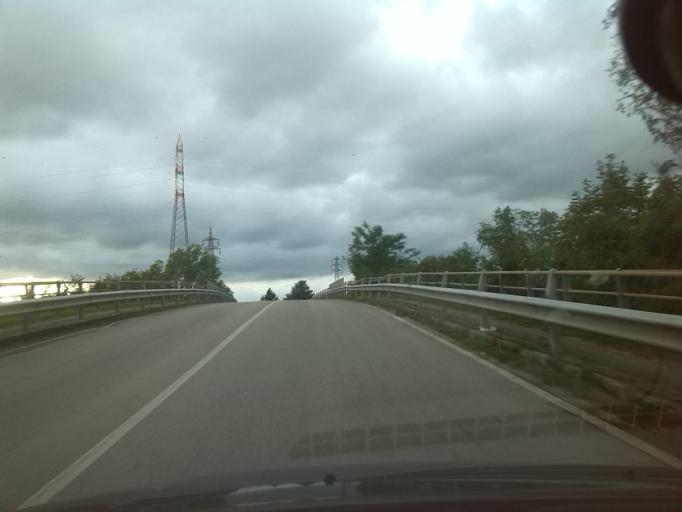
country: IT
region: Friuli Venezia Giulia
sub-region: Provincia di Udine
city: Feletto Umberto
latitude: 46.1009
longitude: 13.2476
